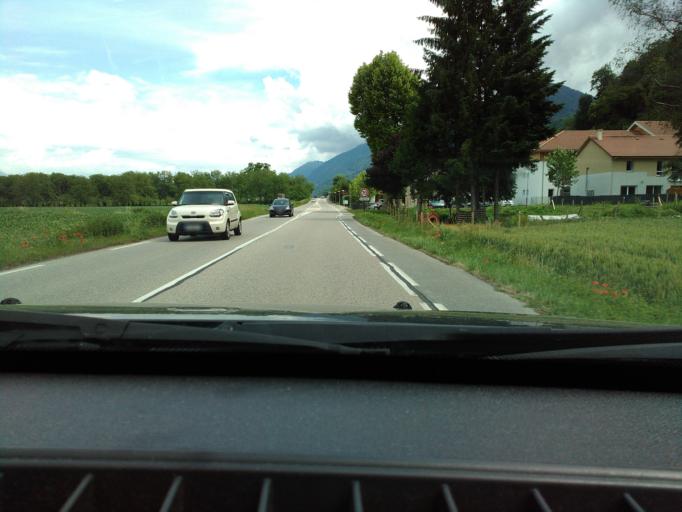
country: FR
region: Rhone-Alpes
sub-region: Departement de l'Isere
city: Le Champ-pres-Froges
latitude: 45.2917
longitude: 5.9421
